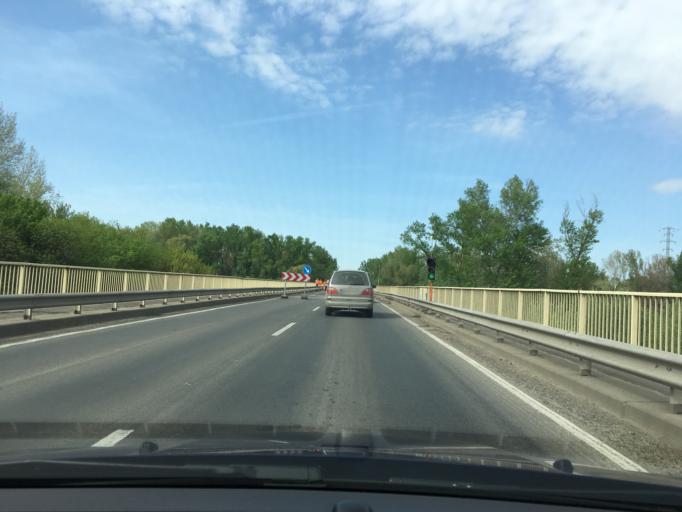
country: HU
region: Csongrad
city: Algyo
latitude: 46.3501
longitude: 20.2064
